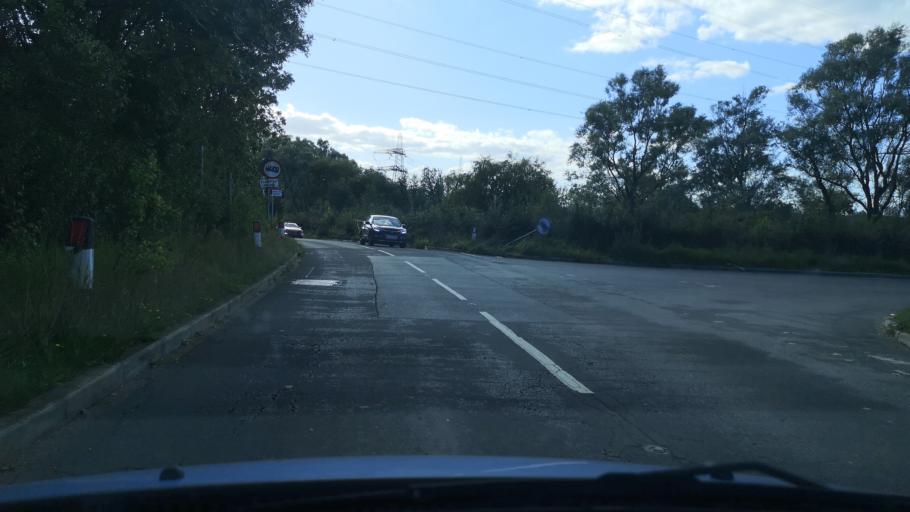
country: GB
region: England
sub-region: Doncaster
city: Kirk Sandall
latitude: 53.5760
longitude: -1.0828
